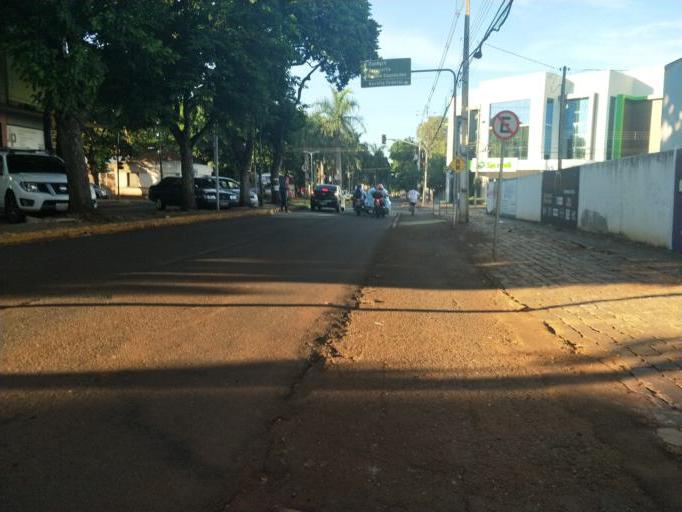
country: BR
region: Parana
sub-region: Marechal Candido Rondon
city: Marechal Candido Rondon
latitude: -24.5593
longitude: -54.0575
